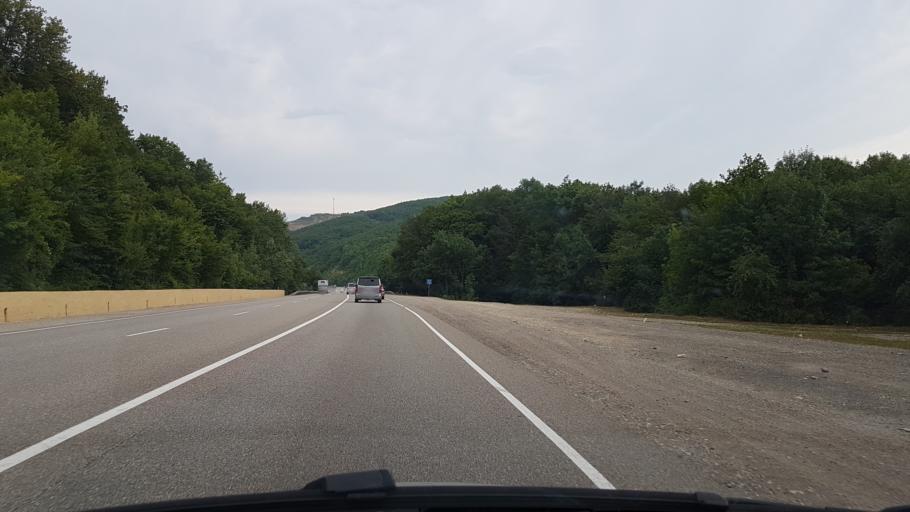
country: RU
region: Krasnodarskiy
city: Goryachiy Klyuch
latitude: 44.5850
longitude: 39.0070
